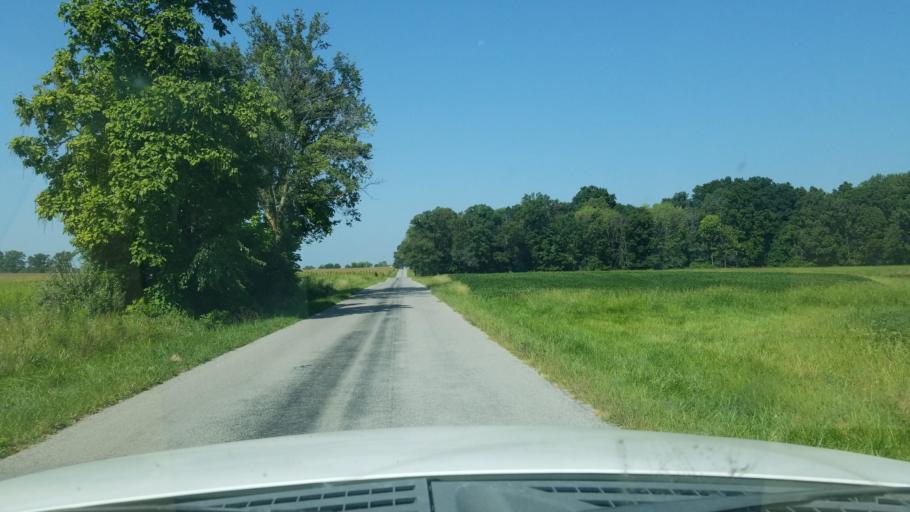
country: US
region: Illinois
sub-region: Saline County
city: Harrisburg
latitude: 37.8924
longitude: -88.6398
